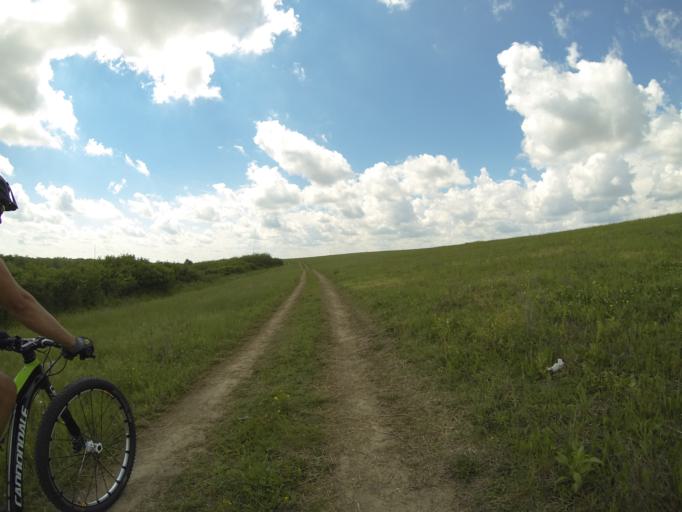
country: RO
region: Dolj
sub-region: Comuna Carcea
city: Carcea
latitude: 44.2666
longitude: 23.8759
